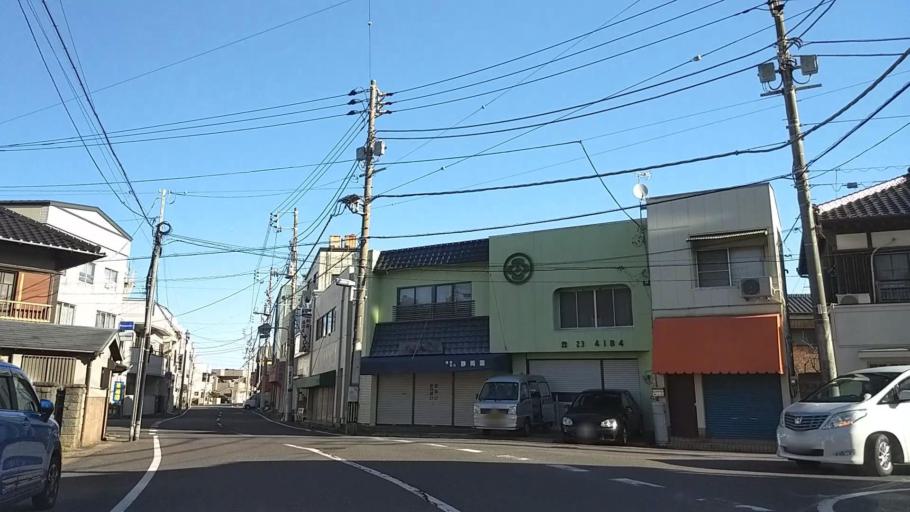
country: JP
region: Chiba
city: Hasaki
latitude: 35.7338
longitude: 140.8466
